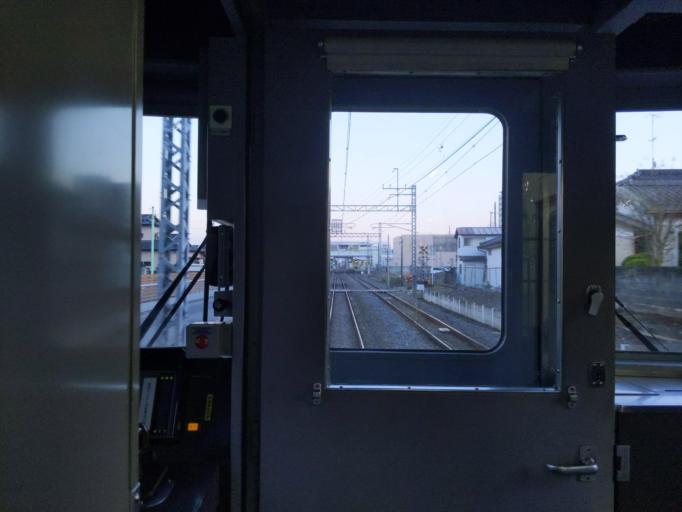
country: JP
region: Chiba
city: Noda
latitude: 35.9328
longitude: 139.8897
